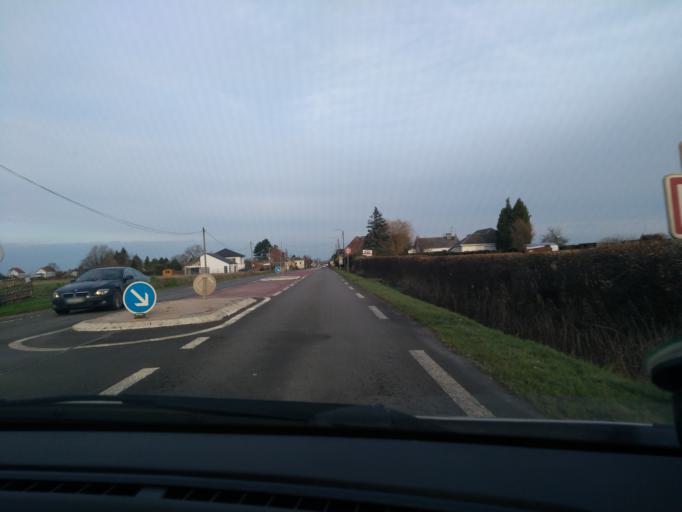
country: FR
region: Nord-Pas-de-Calais
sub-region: Departement du Nord
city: Maubeuge
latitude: 50.3297
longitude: 3.9741
